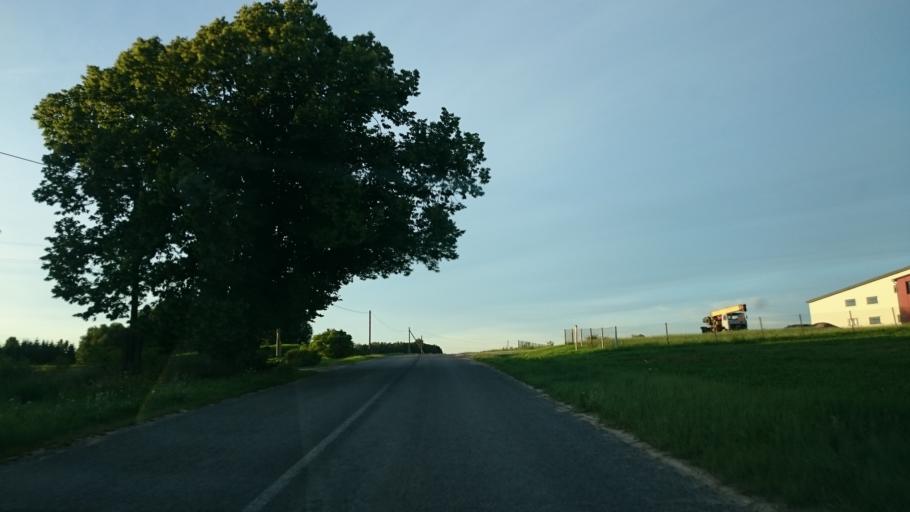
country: LV
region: Saldus Rajons
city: Saldus
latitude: 56.6773
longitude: 22.4956
